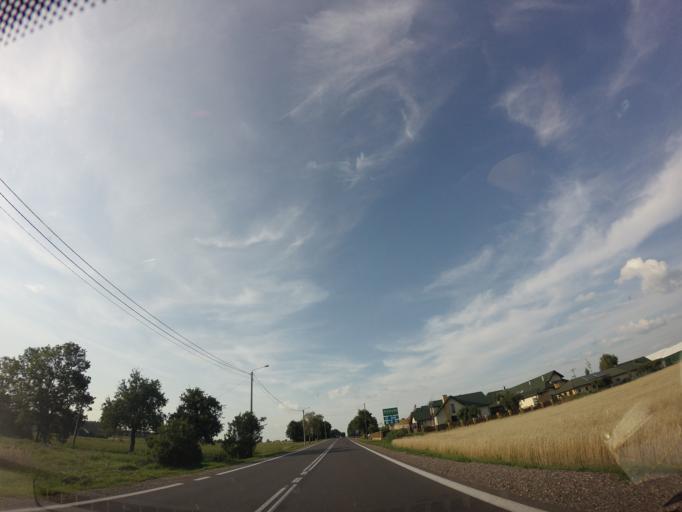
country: PL
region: Podlasie
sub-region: Powiat sokolski
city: Suchowola
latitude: 53.4696
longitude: 23.0901
